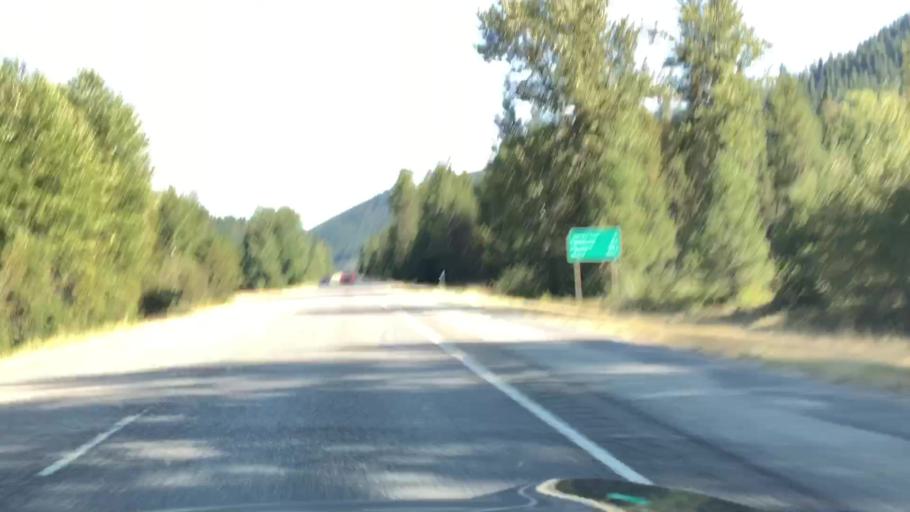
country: US
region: Montana
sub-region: Sanders County
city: Thompson Falls
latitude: 47.3688
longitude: -115.3358
